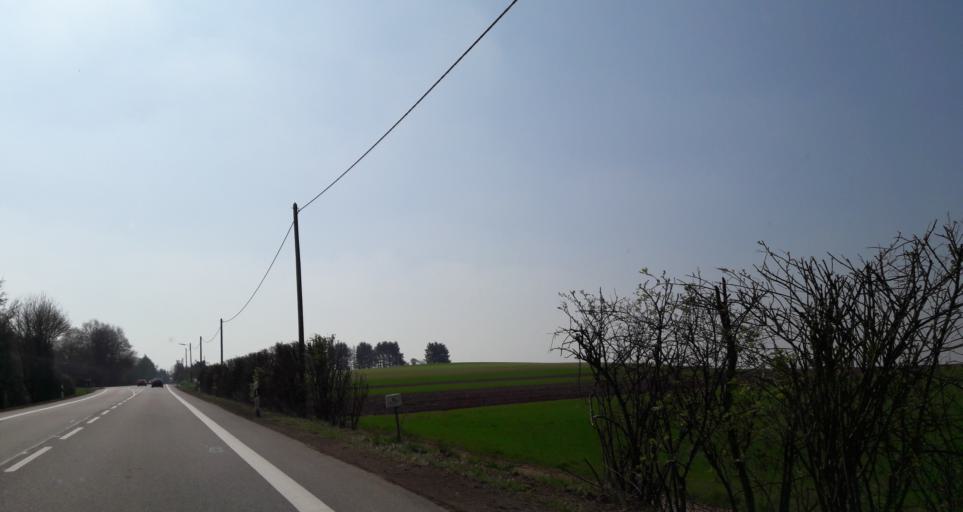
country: DE
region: Saarland
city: Tholey
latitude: 49.5333
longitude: 7.0398
